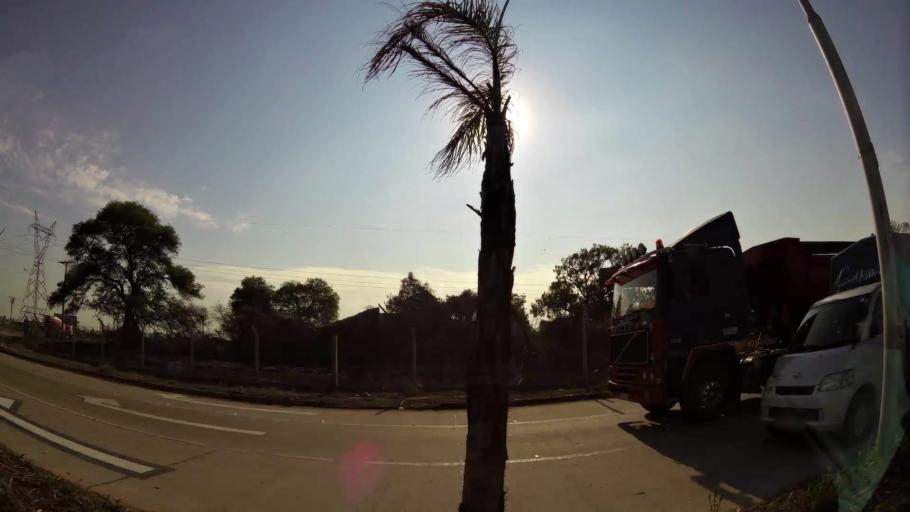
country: BO
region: Santa Cruz
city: Santa Cruz de la Sierra
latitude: -17.7038
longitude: -63.1304
